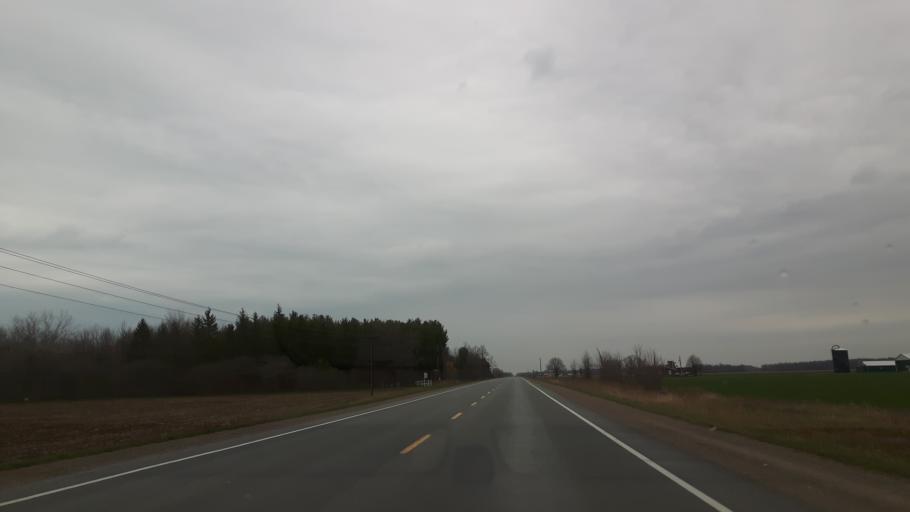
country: CA
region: Ontario
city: Goderich
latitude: 43.6190
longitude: -81.7056
